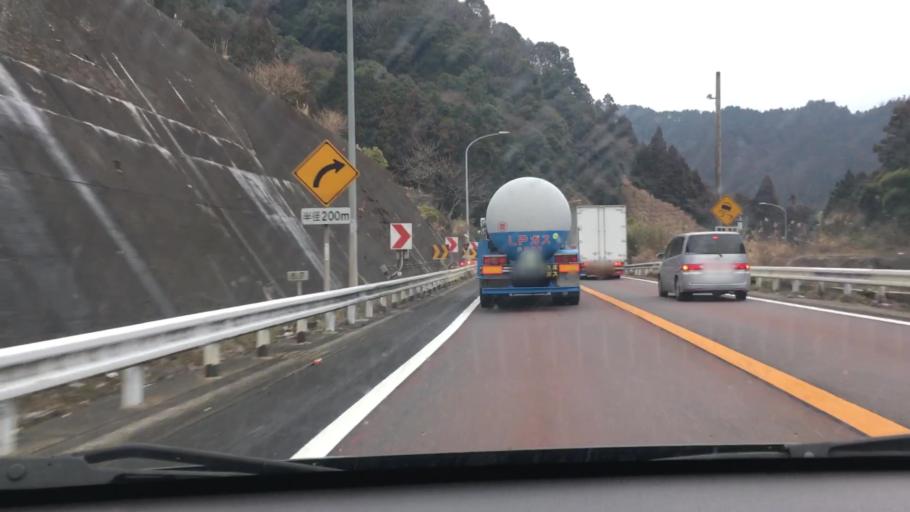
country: JP
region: Mie
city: Kameyama
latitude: 34.8397
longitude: 136.3604
